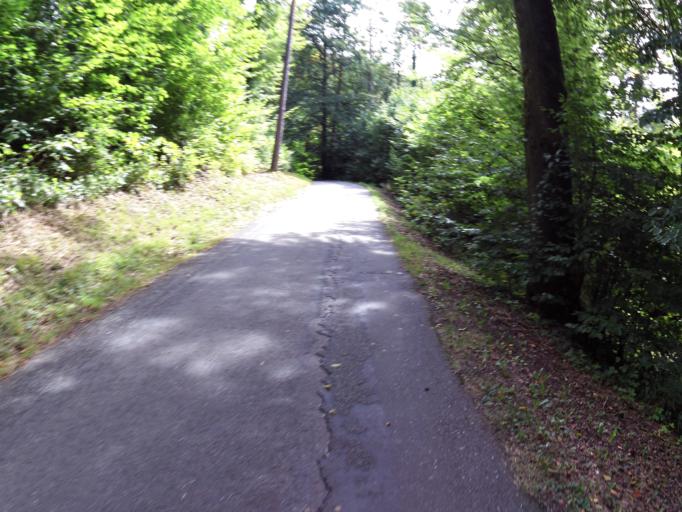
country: DE
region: Baden-Wuerttemberg
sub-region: Freiburg Region
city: Oberndorf
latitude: 48.3243
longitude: 8.5927
